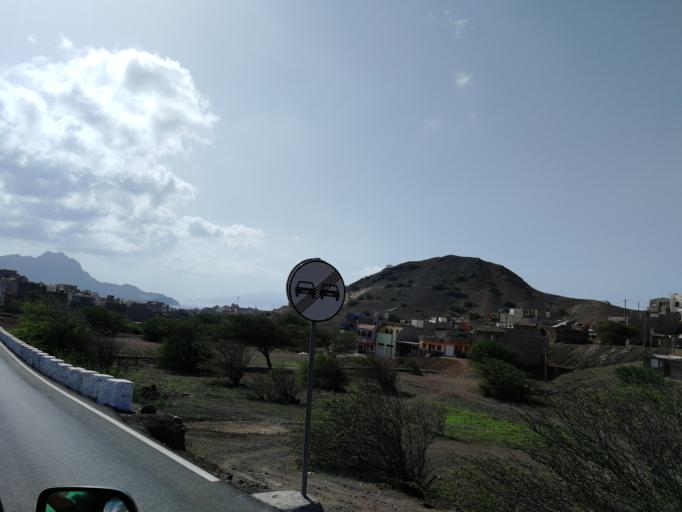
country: CV
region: Sao Vicente
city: Mindelo
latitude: 16.8806
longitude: -24.9684
